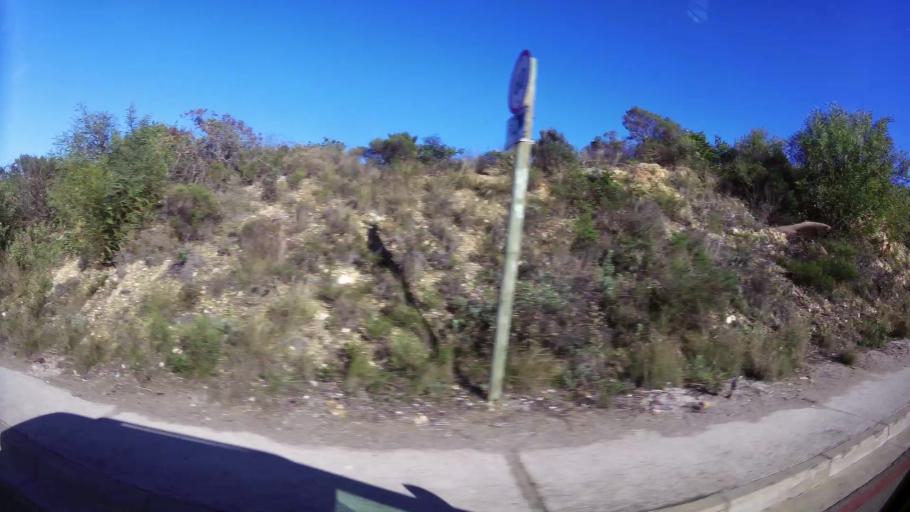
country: ZA
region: Eastern Cape
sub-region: Nelson Mandela Bay Metropolitan Municipality
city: Port Elizabeth
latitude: -33.9806
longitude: 25.6353
